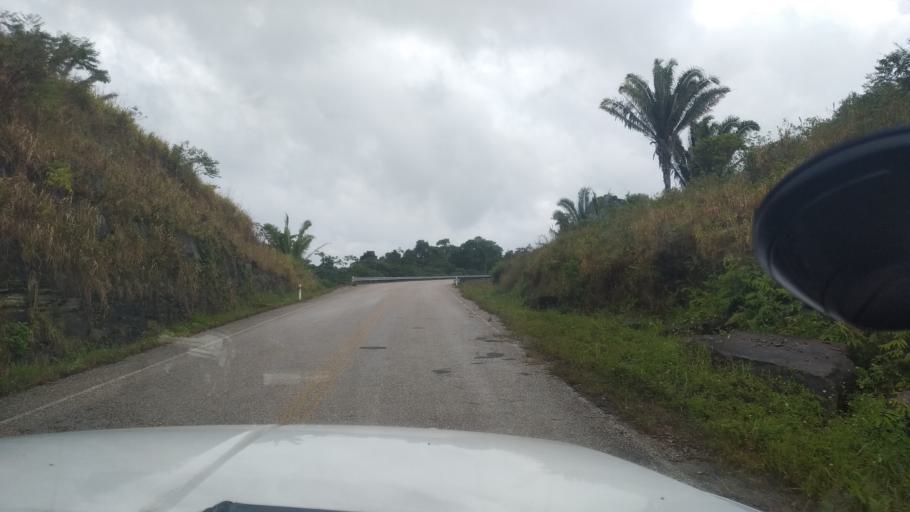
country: GT
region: Peten
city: San Luis
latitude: 16.1955
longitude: -89.1673
